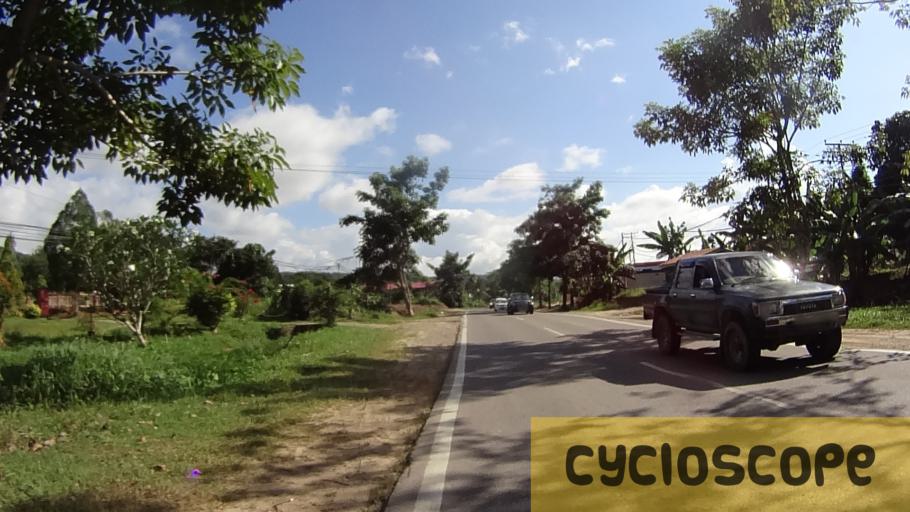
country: MY
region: Sabah
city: Beaufort
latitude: 5.0561
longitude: 115.5497
